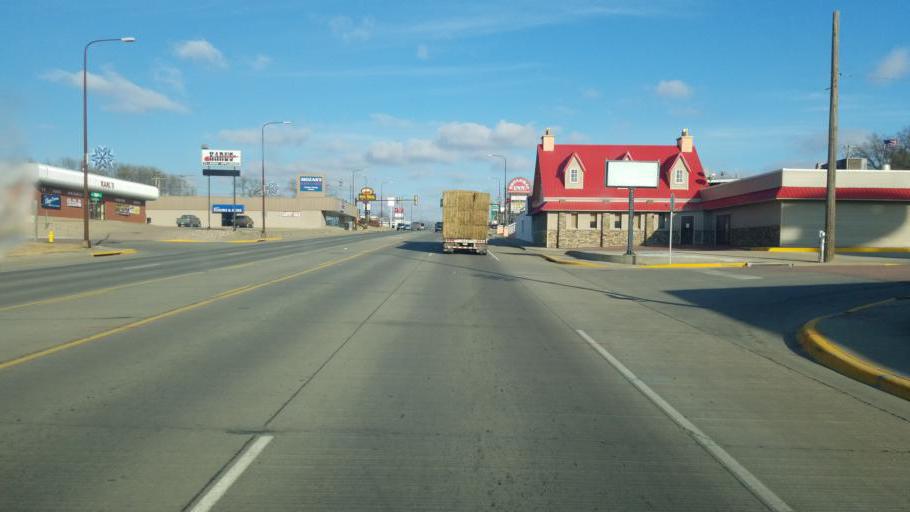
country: US
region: South Dakota
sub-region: Yankton County
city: Yankton
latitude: 42.8820
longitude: -97.3966
